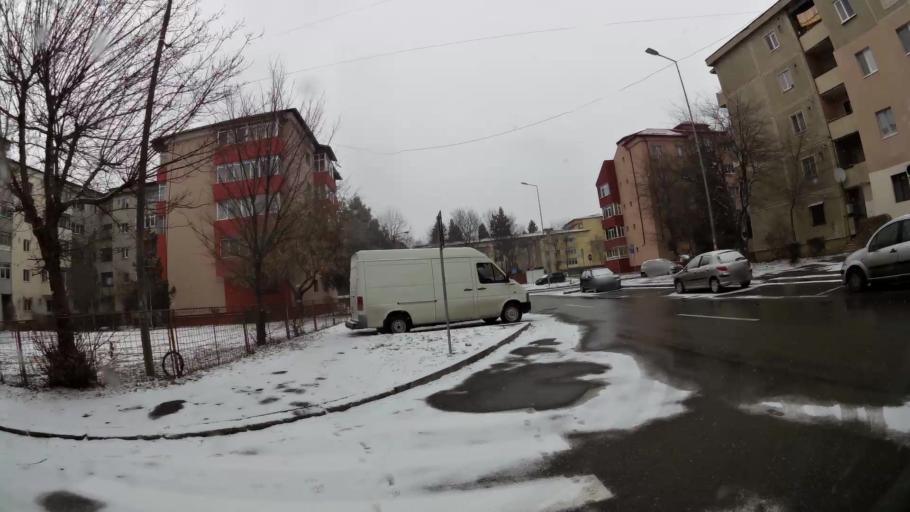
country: RO
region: Dambovita
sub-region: Municipiul Targoviste
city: Targoviste
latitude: 44.9178
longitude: 25.4626
